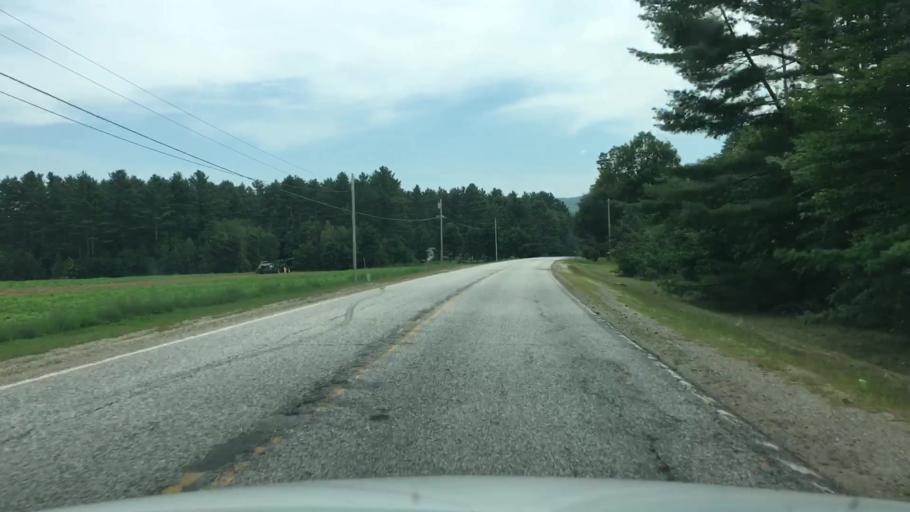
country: US
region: Maine
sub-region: Oxford County
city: Rumford
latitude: 44.5860
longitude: -70.7348
